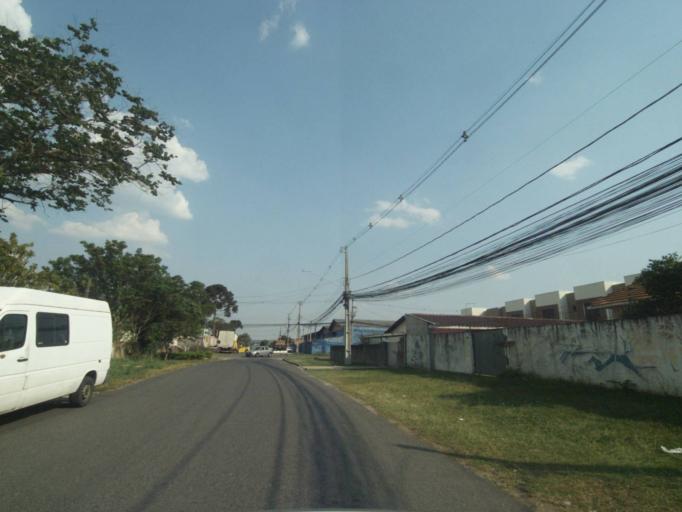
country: BR
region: Parana
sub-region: Sao Jose Dos Pinhais
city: Sao Jose dos Pinhais
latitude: -25.5338
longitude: -49.2357
